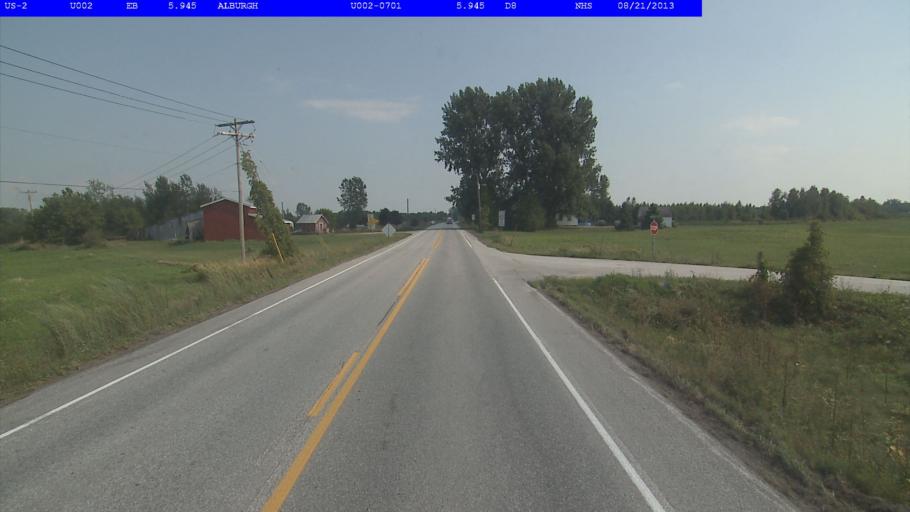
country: US
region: New York
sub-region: Clinton County
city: Rouses Point
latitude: 44.9626
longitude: -73.2813
